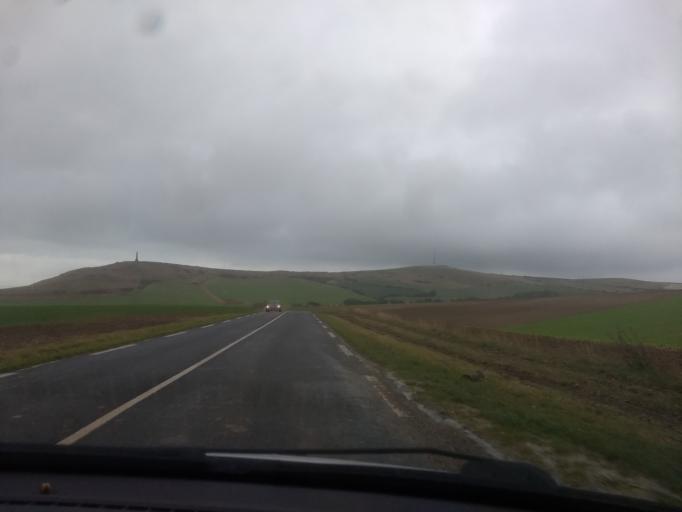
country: FR
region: Nord-Pas-de-Calais
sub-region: Departement du Pas-de-Calais
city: Wissant
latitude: 50.9128
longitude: 1.7020
